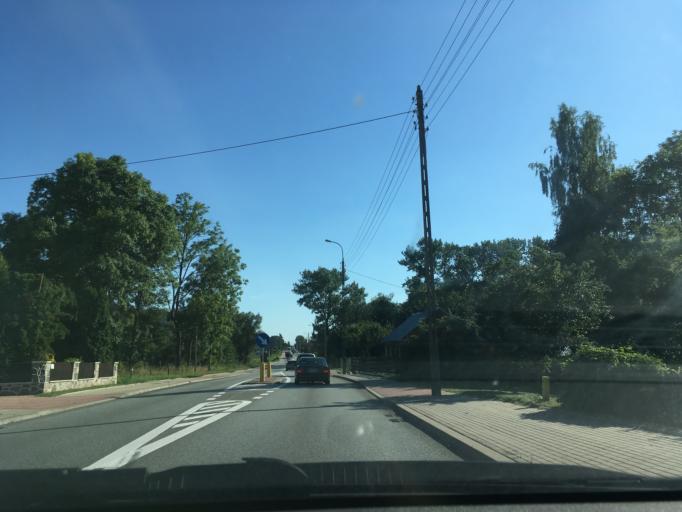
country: PL
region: Podlasie
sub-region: Powiat sokolski
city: Suchowola
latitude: 53.5072
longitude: 23.0988
